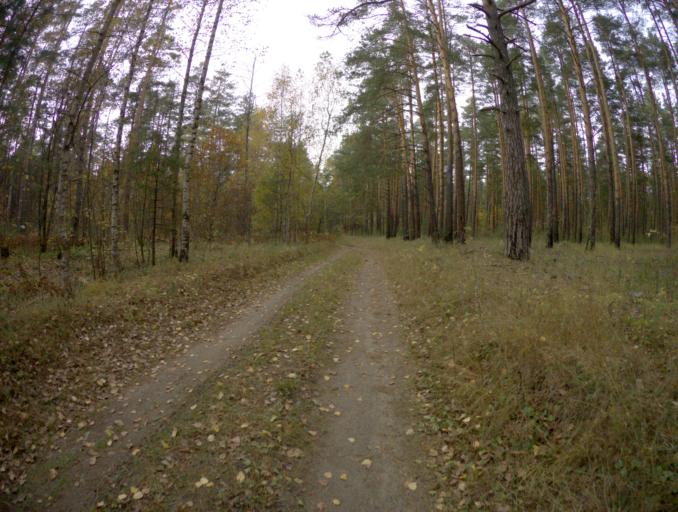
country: RU
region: Vladimir
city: Raduzhnyy
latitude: 56.0325
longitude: 40.3756
